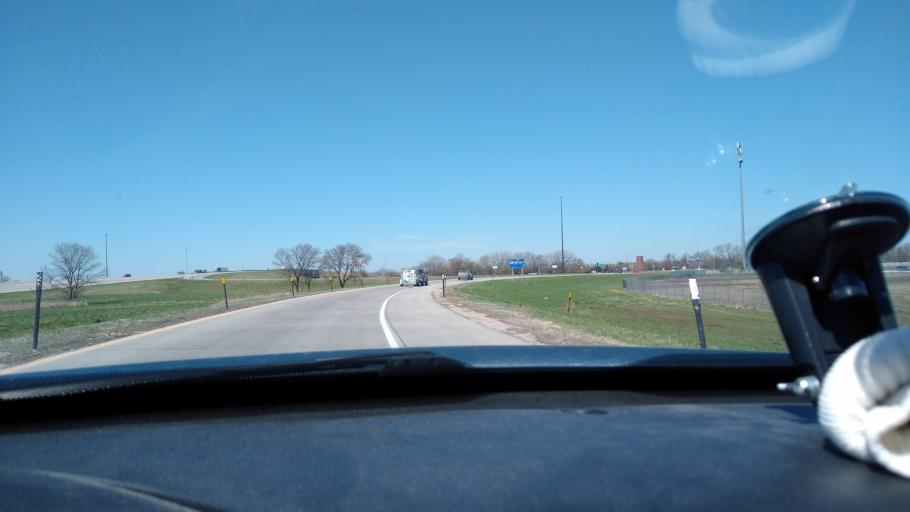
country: US
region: Nebraska
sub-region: Lancaster County
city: Waverly
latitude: 40.8946
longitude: -96.5610
